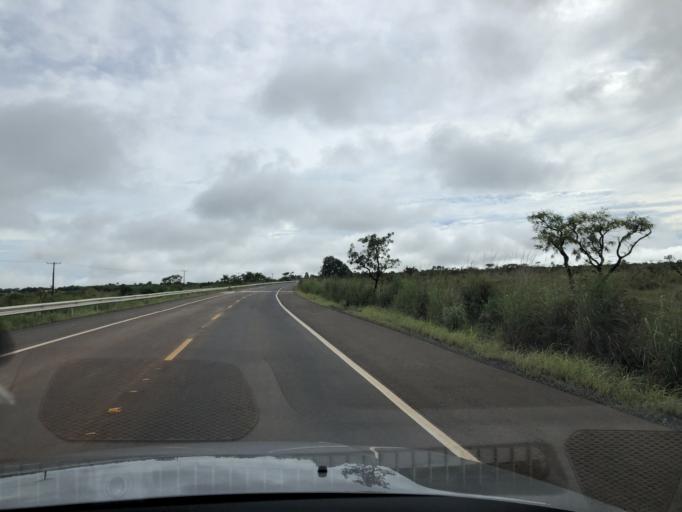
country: BR
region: Federal District
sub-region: Brasilia
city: Brasilia
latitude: -15.6284
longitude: -48.0745
